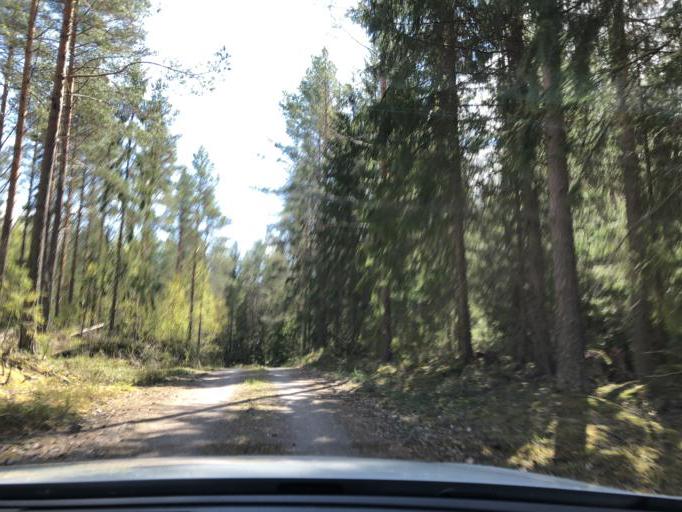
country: SE
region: Uppsala
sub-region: Heby Kommun
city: Tarnsjo
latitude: 60.2379
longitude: 16.7066
